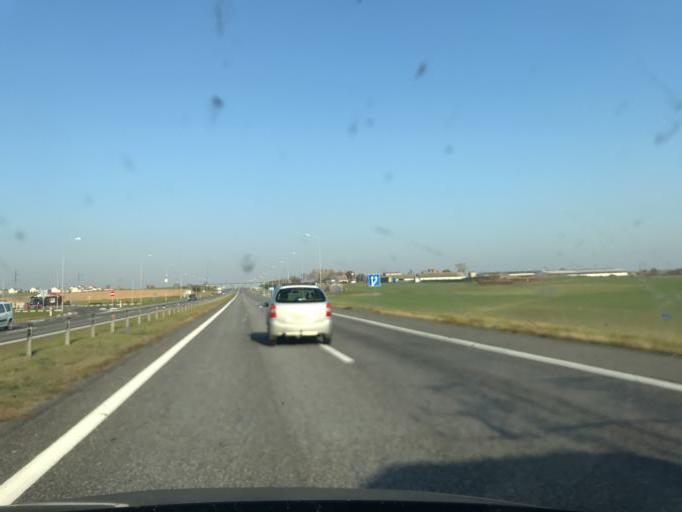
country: BY
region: Minsk
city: Haradzyeya
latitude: 53.3401
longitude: 26.4398
